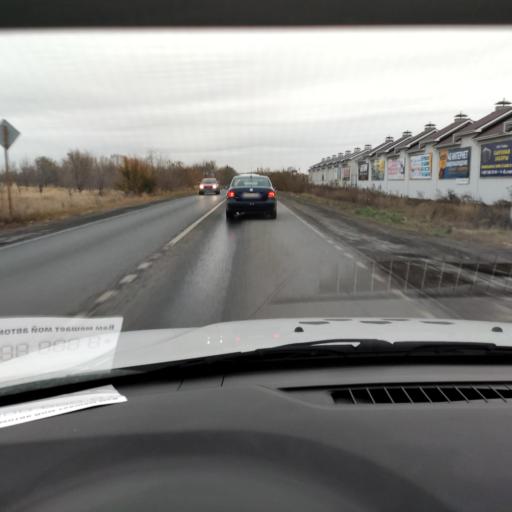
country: RU
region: Samara
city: Podstepki
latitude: 53.5171
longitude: 49.2325
